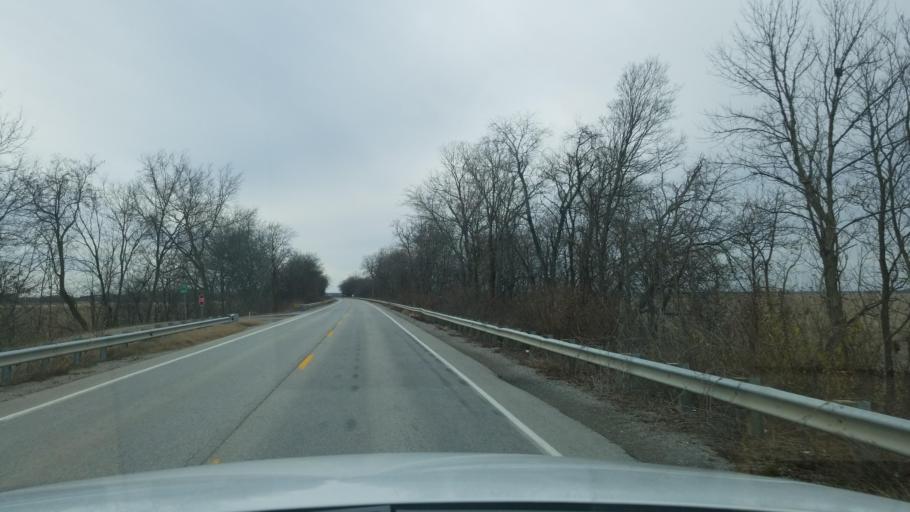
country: US
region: Indiana
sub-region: Posey County
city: Mount Vernon
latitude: 37.9437
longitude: -88.0437
